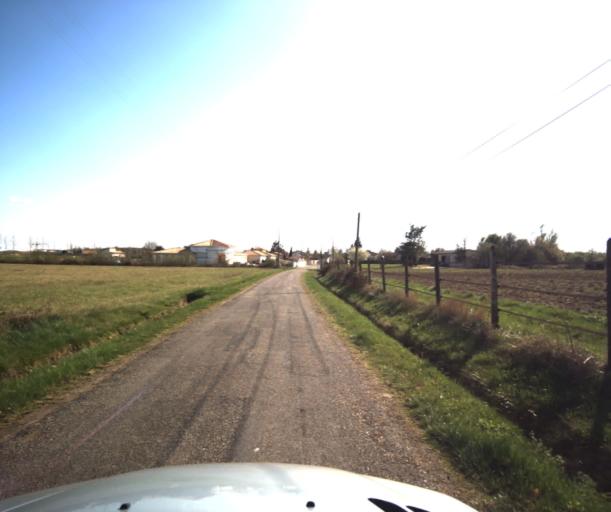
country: FR
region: Midi-Pyrenees
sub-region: Departement du Tarn-et-Garonne
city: Bressols
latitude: 43.9429
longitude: 1.3098
